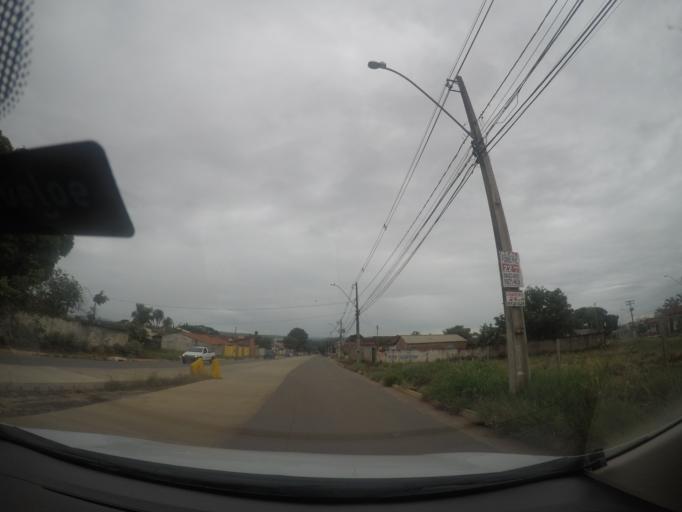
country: BR
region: Goias
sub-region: Goiania
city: Goiania
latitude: -16.6199
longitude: -49.3028
